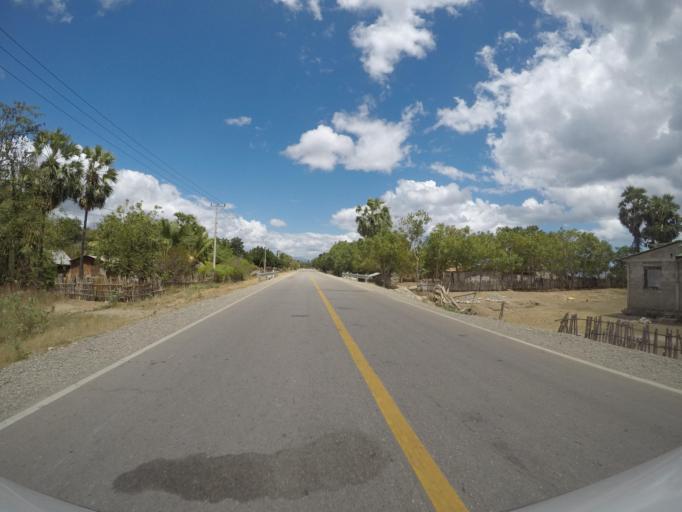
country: TL
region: Lautem
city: Lospalos
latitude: -8.3752
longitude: 126.8733
